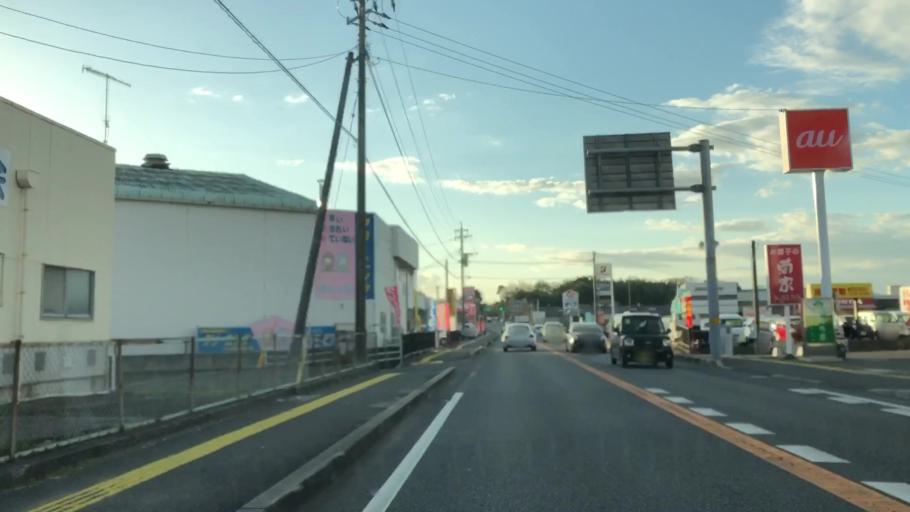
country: JP
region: Oita
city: Bungo-Takada-shi
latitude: 33.5349
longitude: 131.3218
